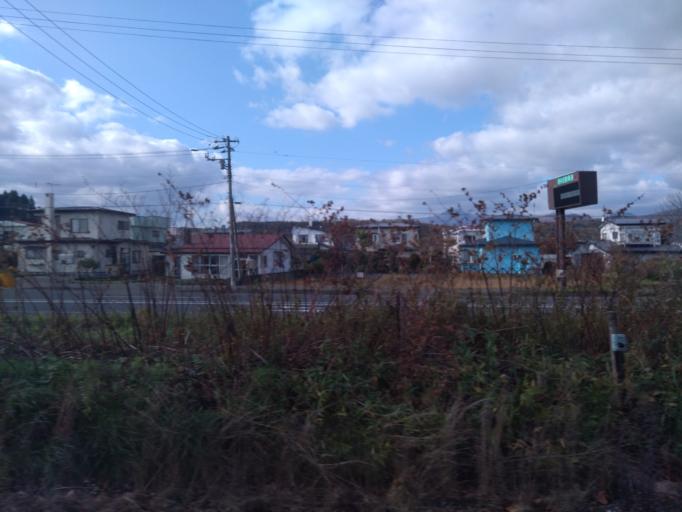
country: JP
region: Hokkaido
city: Shiraoi
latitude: 42.4475
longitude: 141.1737
